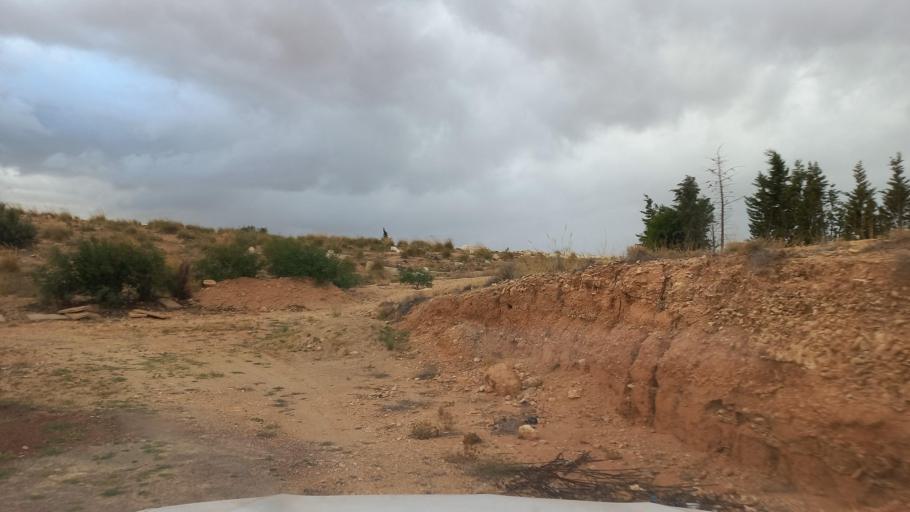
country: TN
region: Al Qasrayn
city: Kasserine
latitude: 35.2777
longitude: 8.9370
